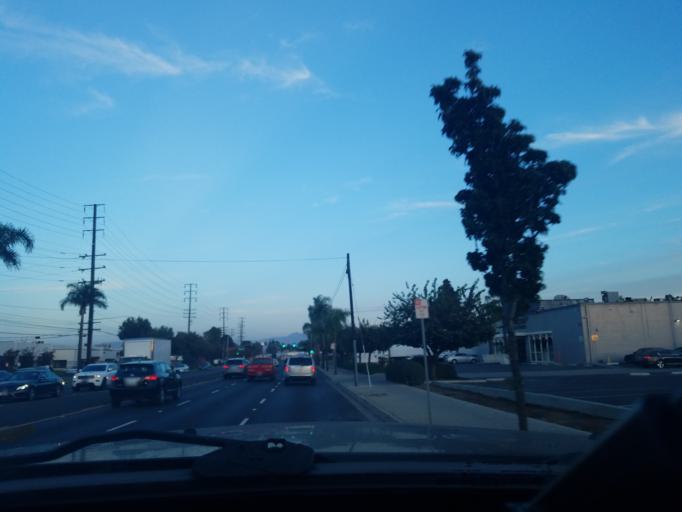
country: US
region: California
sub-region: Orange County
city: Fountain Valley
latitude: 33.7138
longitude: -117.9182
